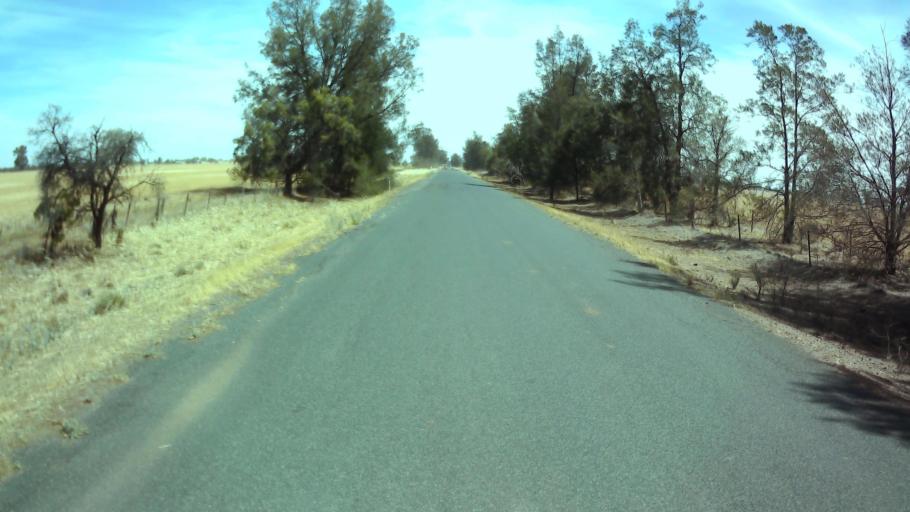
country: AU
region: New South Wales
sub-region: Weddin
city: Grenfell
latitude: -33.9221
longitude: 147.7639
